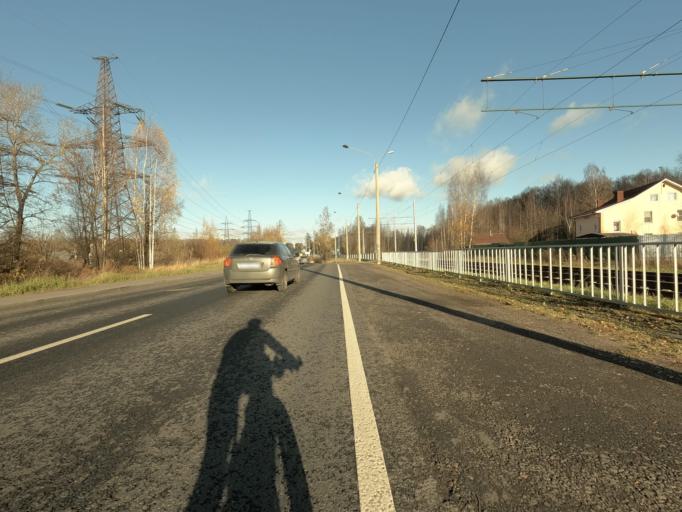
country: RU
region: St.-Petersburg
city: Krasnogvargeisky
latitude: 59.9671
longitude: 30.5020
